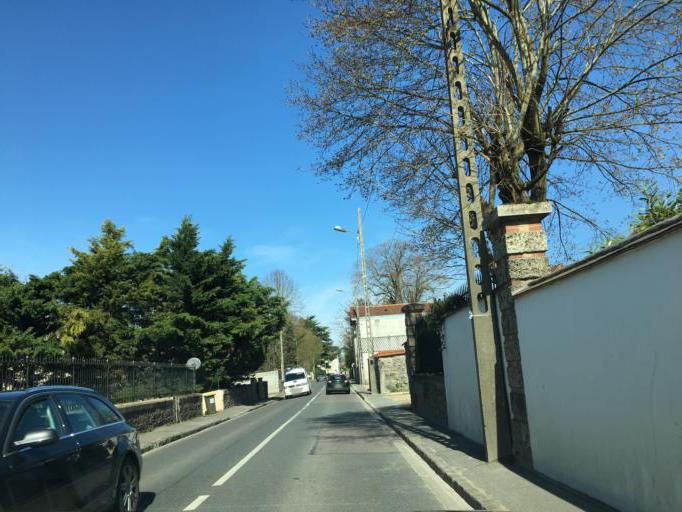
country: FR
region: Ile-de-France
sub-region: Departement de l'Essonne
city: Draveil
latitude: 48.6692
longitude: 2.4151
